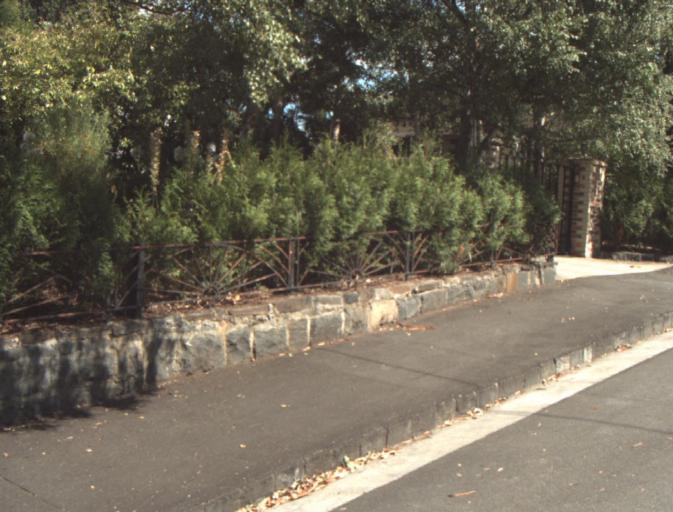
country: AU
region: Tasmania
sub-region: Launceston
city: Launceston
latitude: -41.4229
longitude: 147.1386
